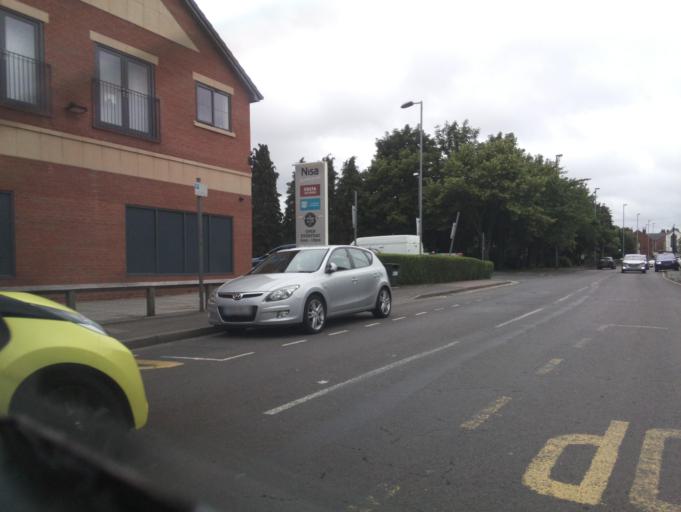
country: GB
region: England
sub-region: Staffordshire
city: Burton upon Trent
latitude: 52.8217
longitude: -1.6413
